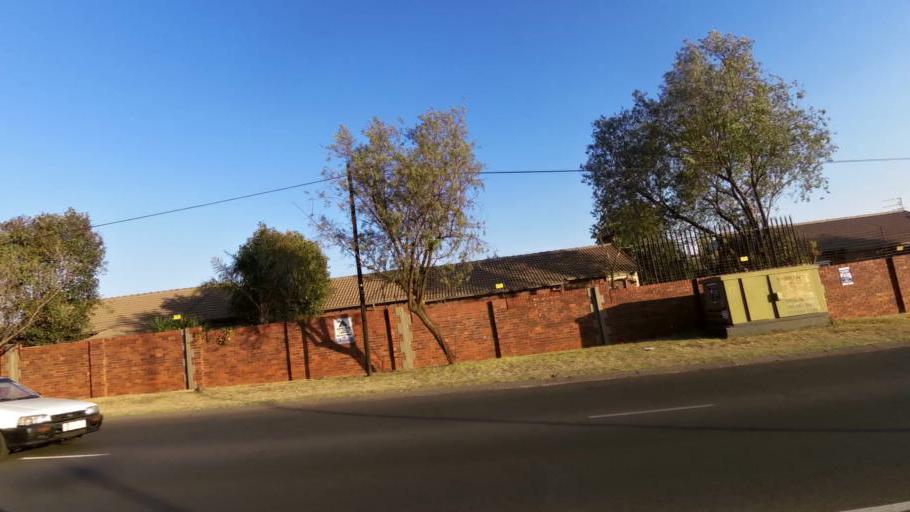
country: ZA
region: Gauteng
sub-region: City of Johannesburg Metropolitan Municipality
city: Roodepoort
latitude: -26.1641
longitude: 27.9504
